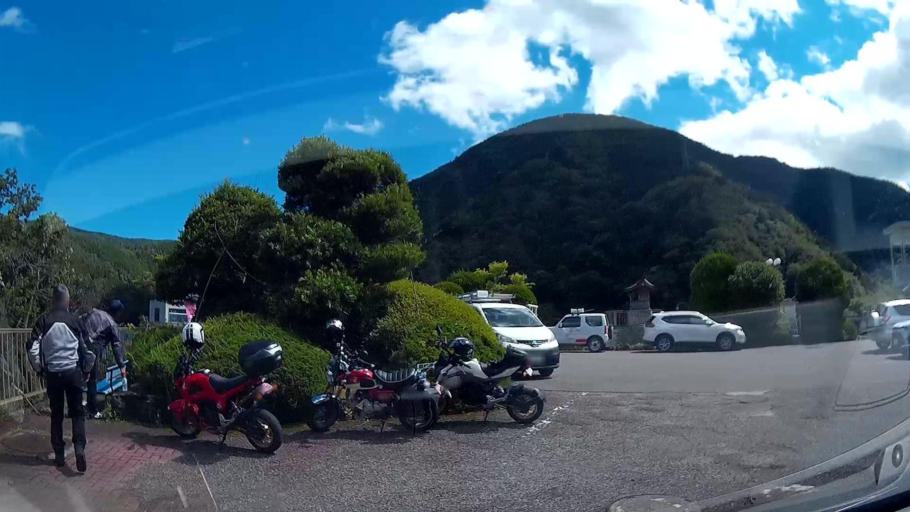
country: JP
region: Shizuoka
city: Shizuoka-shi
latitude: 35.2112
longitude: 138.2243
